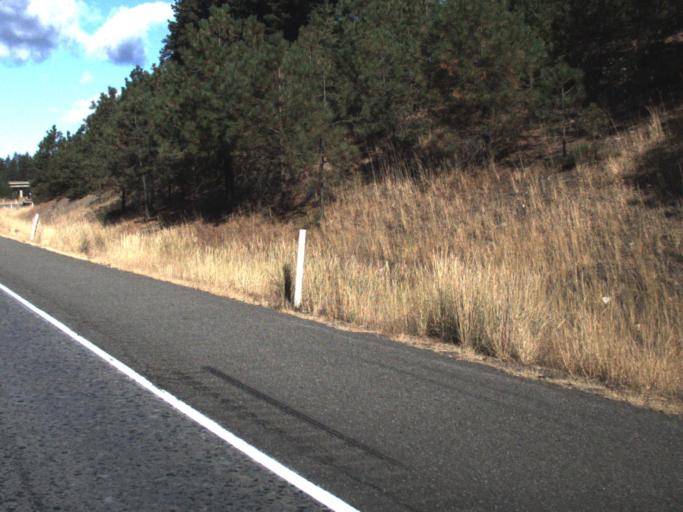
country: US
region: Washington
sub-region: Kittitas County
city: Cle Elum
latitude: 47.1933
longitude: -120.9531
